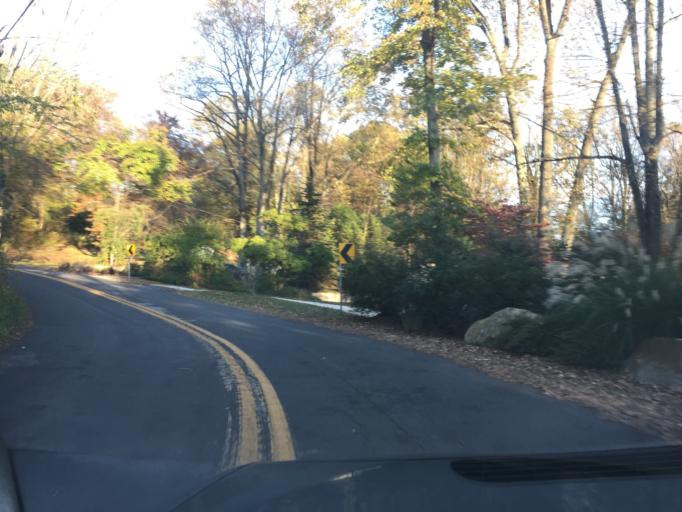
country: US
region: Maryland
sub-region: Baltimore County
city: Hampton
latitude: 39.4732
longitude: -76.5319
